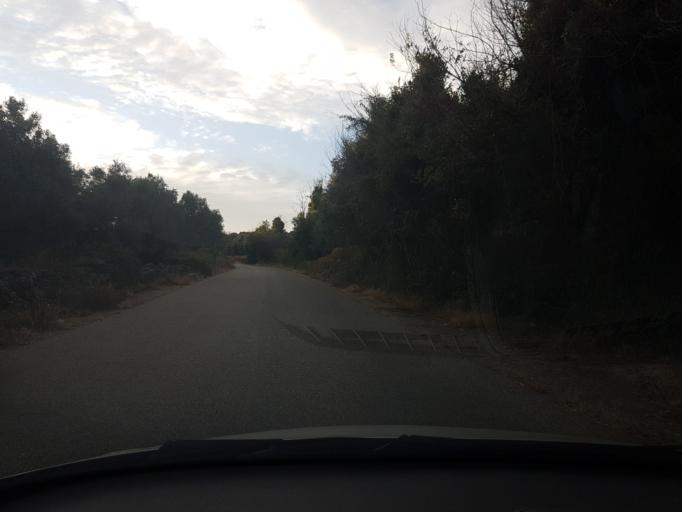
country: IT
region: Sardinia
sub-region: Provincia di Oristano
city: Seneghe
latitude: 40.0974
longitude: 8.6273
